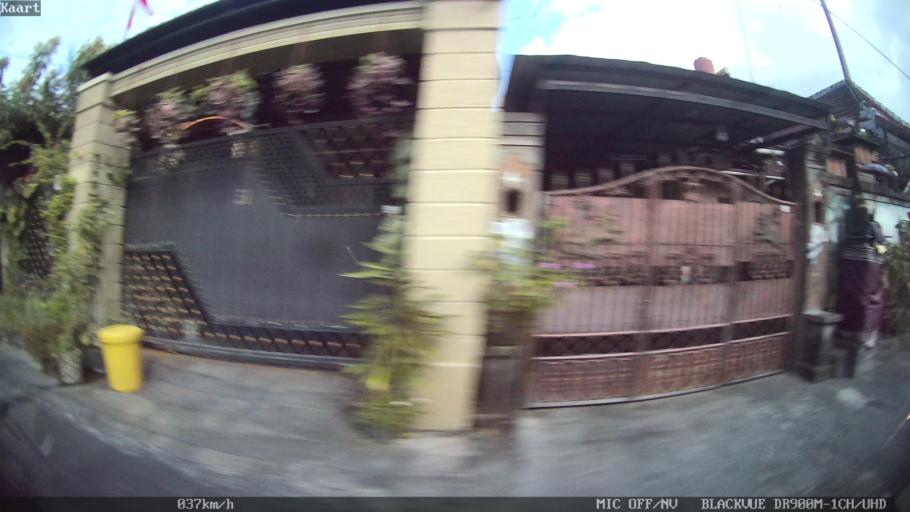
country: ID
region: Bali
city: Karyadharma
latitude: -8.7017
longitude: 115.1938
